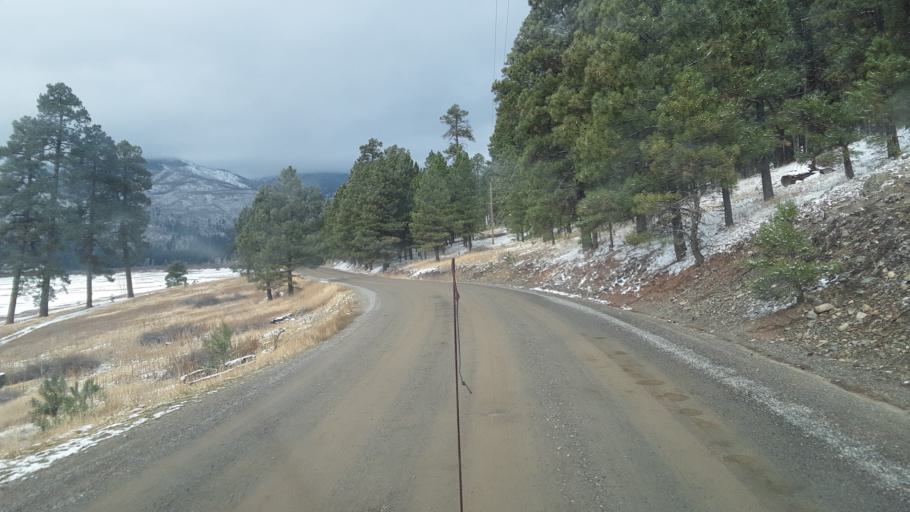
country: US
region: Colorado
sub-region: La Plata County
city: Bayfield
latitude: 37.4261
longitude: -107.5379
